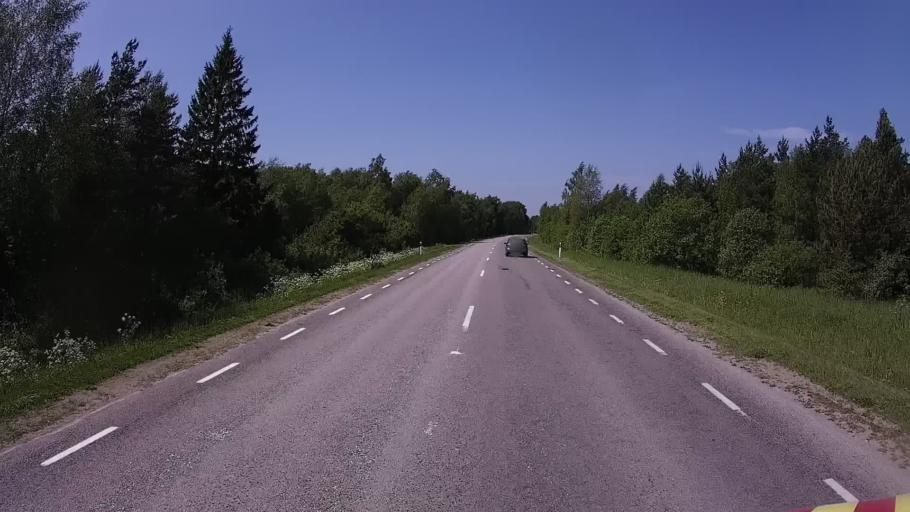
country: EE
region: Saare
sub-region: Kuressaare linn
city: Kuressaare
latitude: 58.2777
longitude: 22.4392
